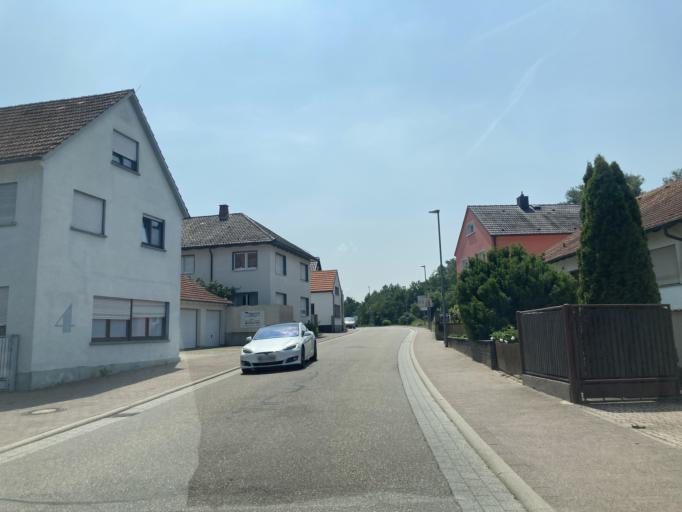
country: DE
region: Baden-Wuerttemberg
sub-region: Karlsruhe Region
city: Linkenheim-Hochstetten
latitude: 49.1399
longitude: 8.4087
